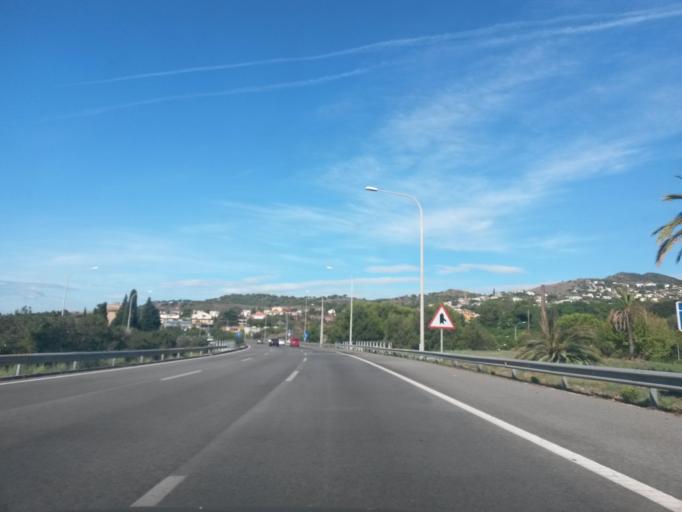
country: ES
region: Catalonia
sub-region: Provincia de Barcelona
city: Alella
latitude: 41.4894
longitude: 2.3033
